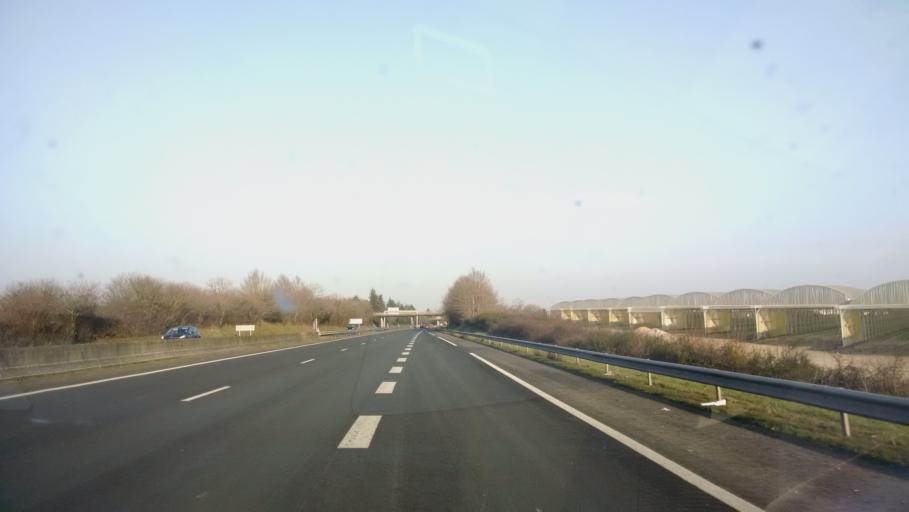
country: FR
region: Pays de la Loire
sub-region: Departement de la Loire-Atlantique
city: Les Sorinieres
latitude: 47.1338
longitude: -1.5083
